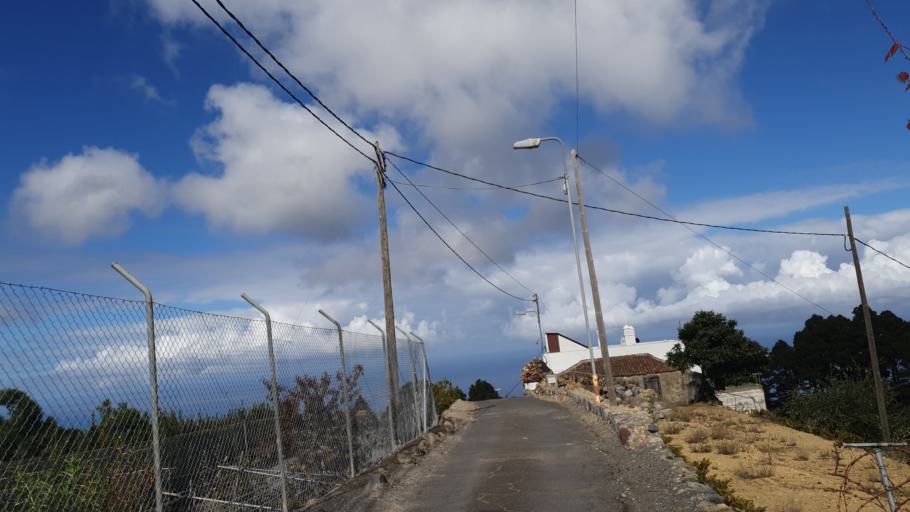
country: ES
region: Canary Islands
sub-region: Provincia de Santa Cruz de Tenerife
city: Icod de los Vinos
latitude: 28.3536
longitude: -16.6862
